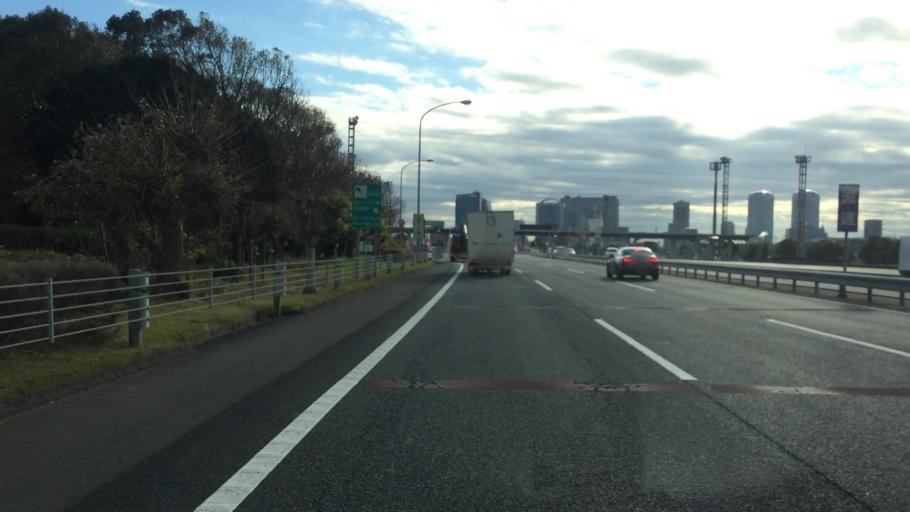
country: JP
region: Chiba
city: Funabashi
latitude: 35.6625
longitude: 140.0227
